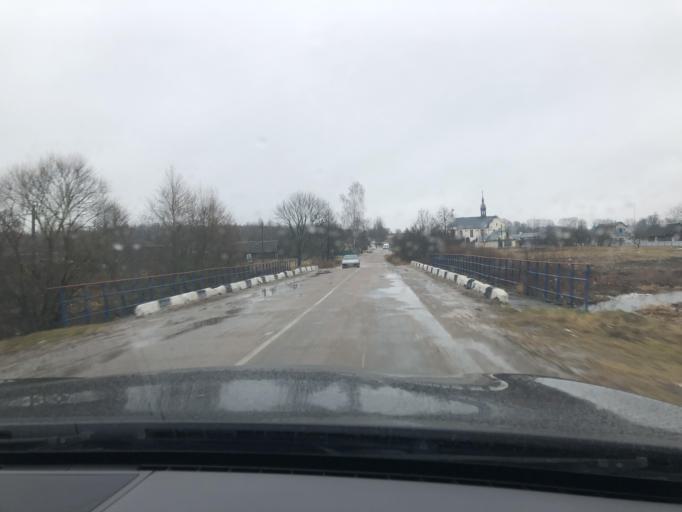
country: BY
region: Grodnenskaya
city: Hal'shany
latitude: 54.1751
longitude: 26.1055
